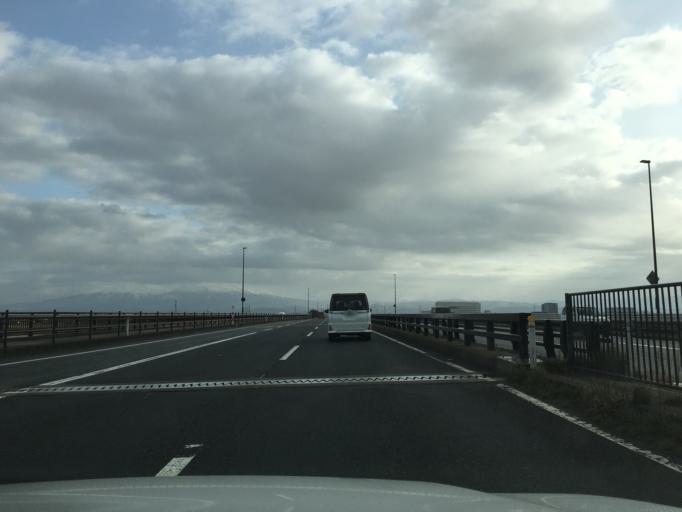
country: JP
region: Yamagata
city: Sakata
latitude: 38.8851
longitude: 139.8403
